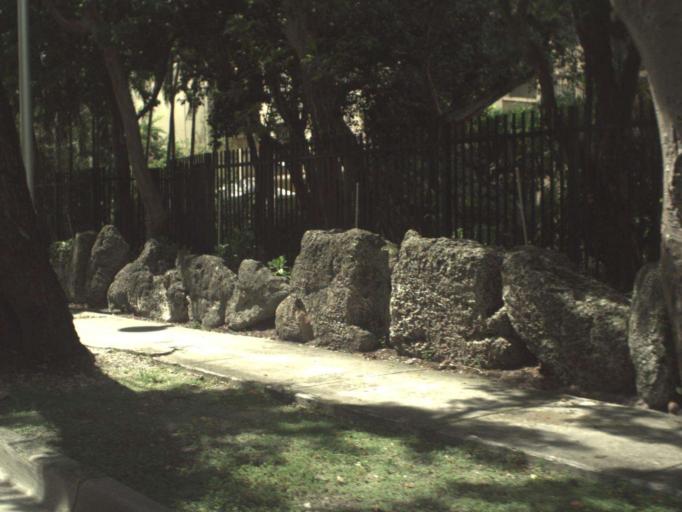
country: US
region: Florida
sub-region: Miami-Dade County
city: Miami
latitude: 25.7517
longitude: -80.2021
